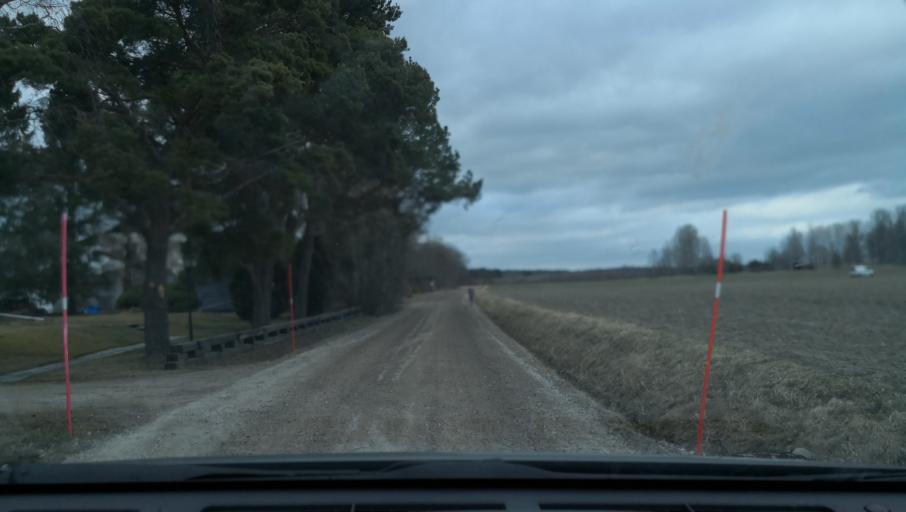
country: SE
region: Vaestmanland
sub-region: Kopings Kommun
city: Kolsva
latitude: 59.5398
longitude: 15.8928
